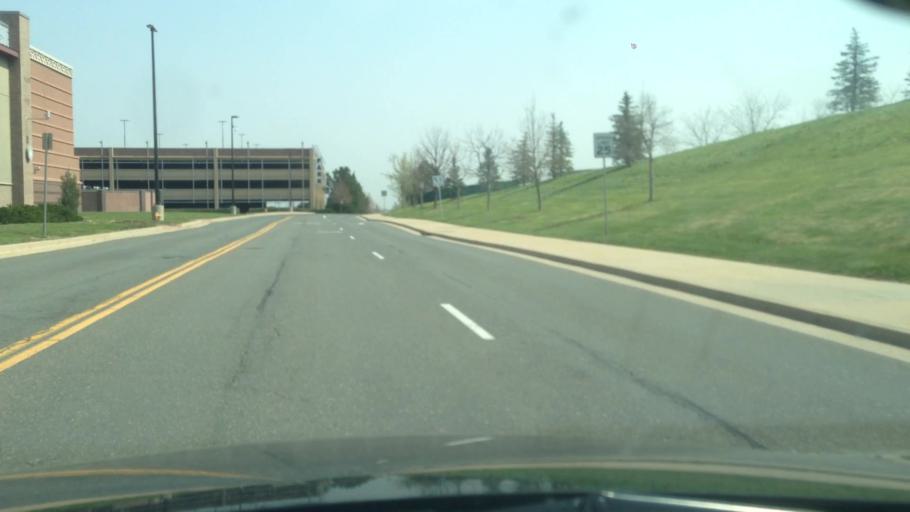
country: US
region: Colorado
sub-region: Jefferson County
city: West Pleasant View
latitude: 39.7311
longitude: -105.1550
